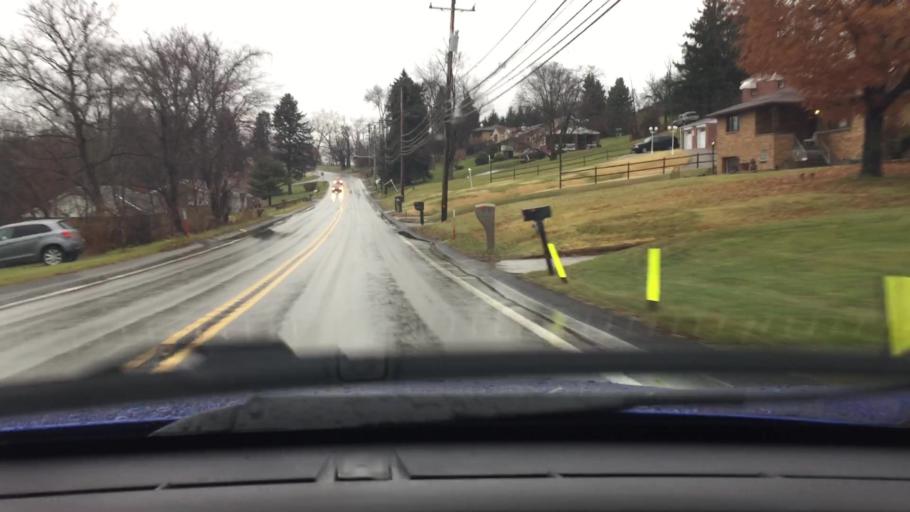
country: US
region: Pennsylvania
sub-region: Allegheny County
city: Wilson
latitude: 40.3133
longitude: -79.9168
